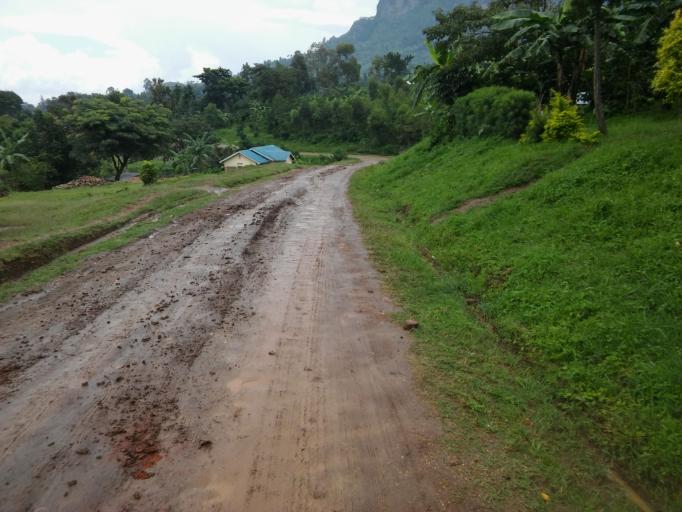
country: UG
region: Eastern Region
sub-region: Mbale District
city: Mbale
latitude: 1.0186
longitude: 34.2206
